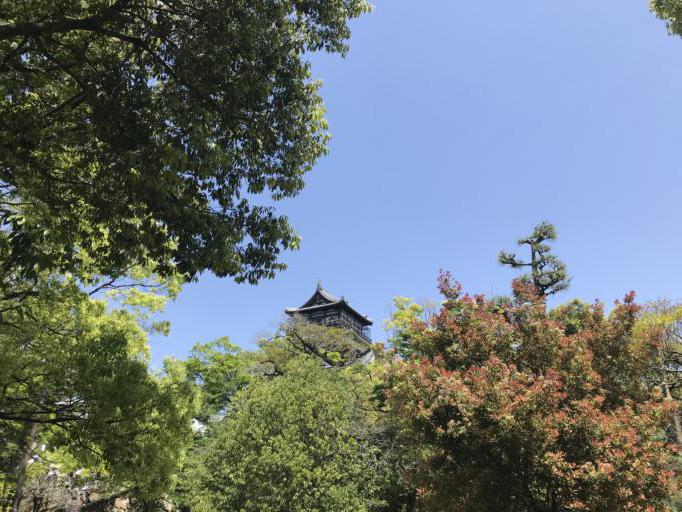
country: JP
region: Hiroshima
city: Hiroshima-shi
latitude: 34.4021
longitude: 132.4593
